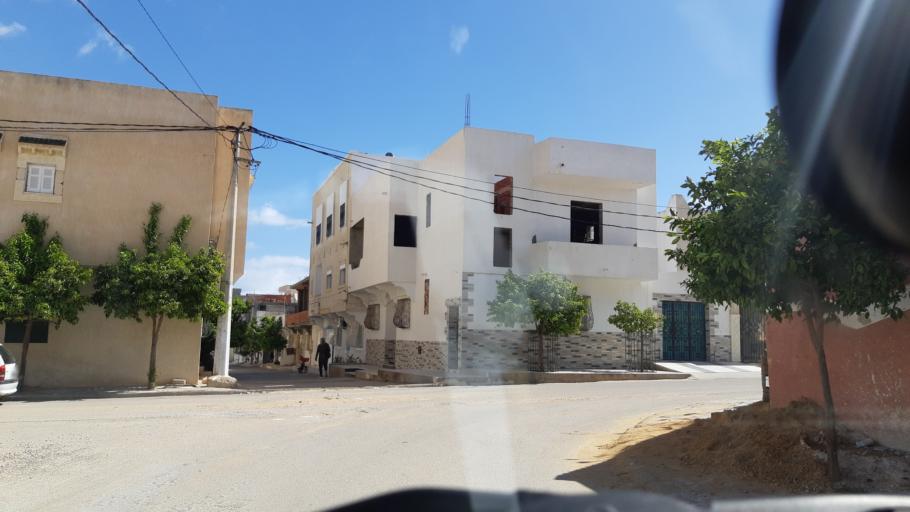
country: TN
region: Susah
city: Akouda
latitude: 35.8910
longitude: 10.5329
